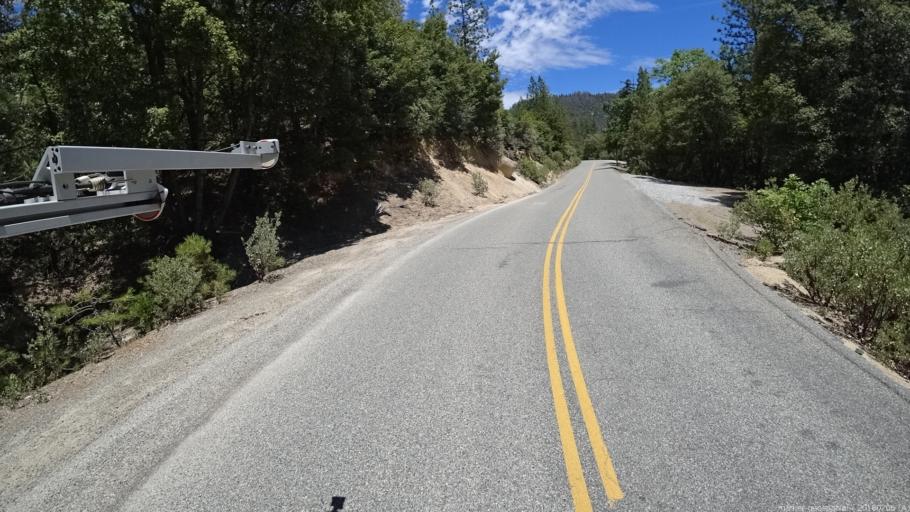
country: US
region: California
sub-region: Madera County
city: Oakhurst
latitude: 37.3537
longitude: -119.5494
